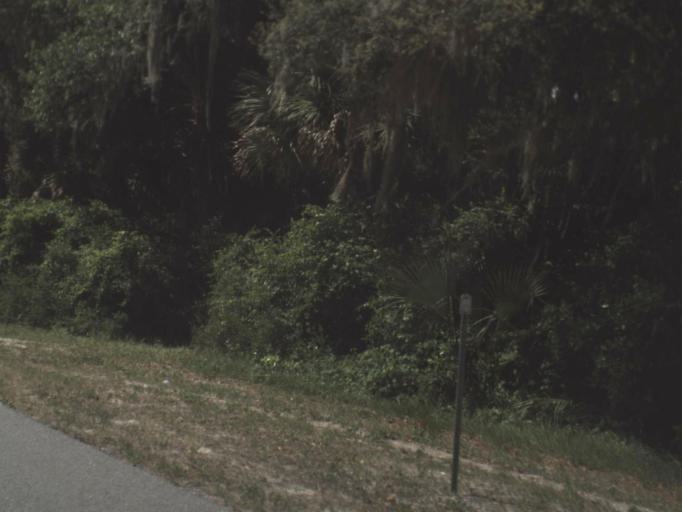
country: US
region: Florida
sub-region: Duval County
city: Atlantic Beach
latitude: 30.4597
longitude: -81.4203
